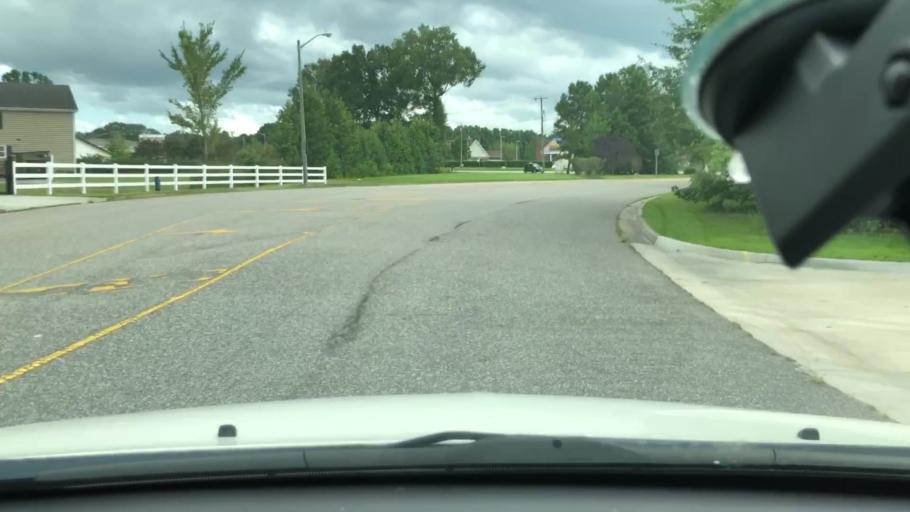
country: US
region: Virginia
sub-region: City of Chesapeake
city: Chesapeake
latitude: 36.7157
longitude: -76.2810
